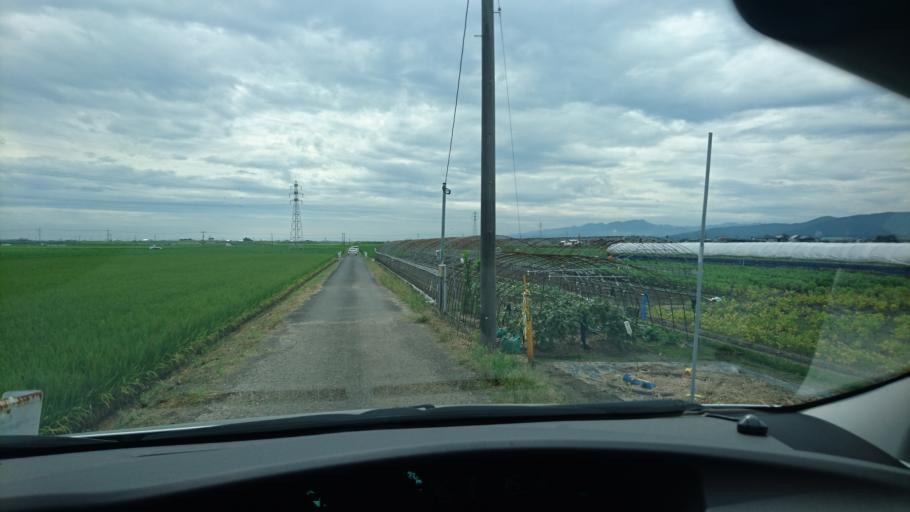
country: JP
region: Saga Prefecture
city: Takeocho-takeo
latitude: 33.2134
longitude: 130.1255
